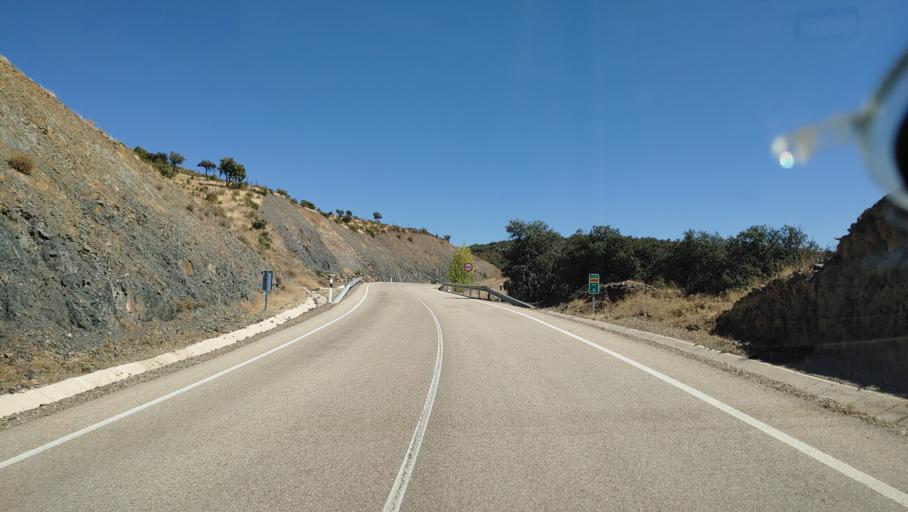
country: ES
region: Andalusia
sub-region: Provincia de Jaen
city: Genave
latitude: 38.5042
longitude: -2.7784
